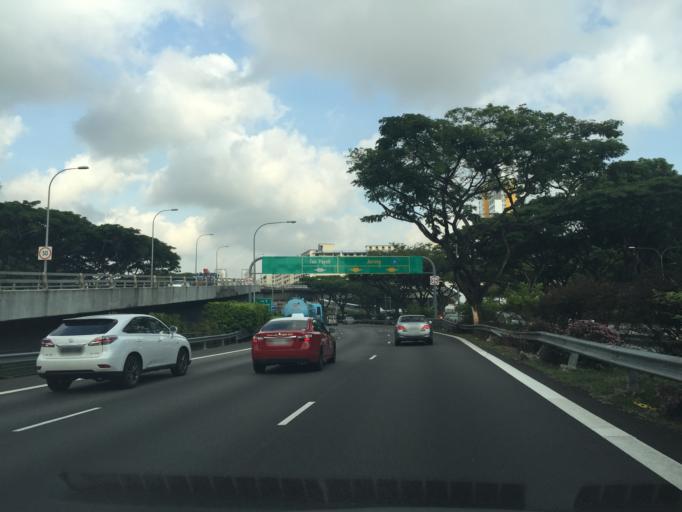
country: SG
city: Singapore
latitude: 1.3304
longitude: 103.8620
